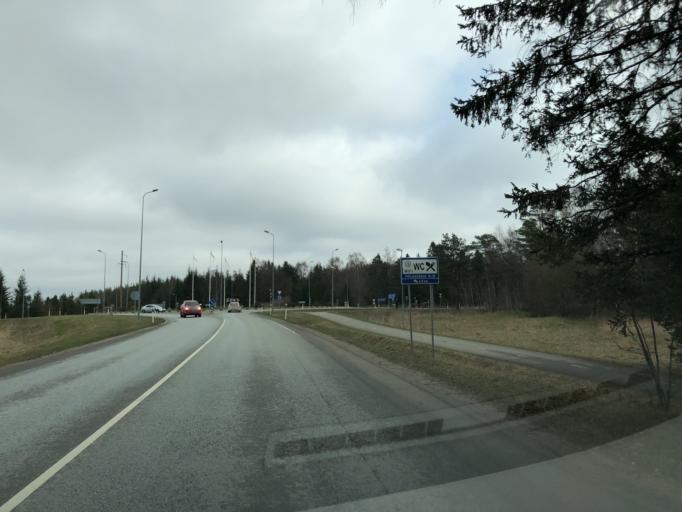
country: EE
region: Laeaene-Virumaa
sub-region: Rakvere linn
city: Rakvere
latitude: 59.3249
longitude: 26.3487
